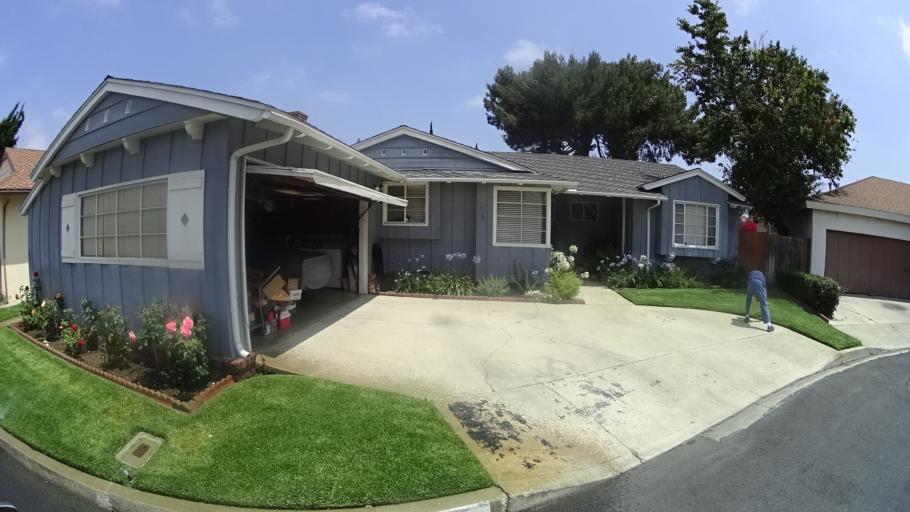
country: US
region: California
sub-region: Los Angeles County
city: View Park-Windsor Hills
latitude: 34.0053
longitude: -118.3525
